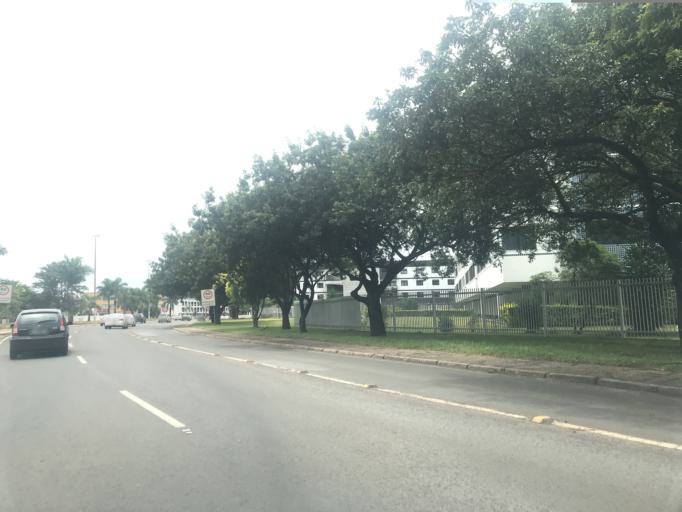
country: BR
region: Federal District
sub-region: Brasilia
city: Brasilia
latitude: -15.8188
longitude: -47.9833
